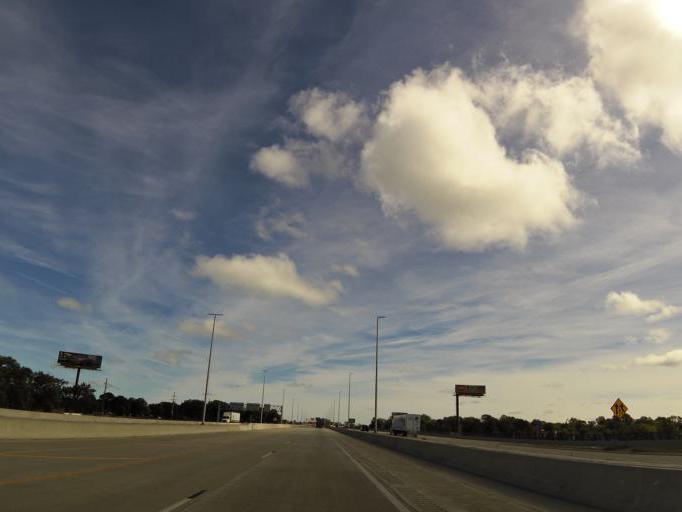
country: US
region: Michigan
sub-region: Saint Clair County
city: Port Huron
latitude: 42.9923
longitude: -82.4496
